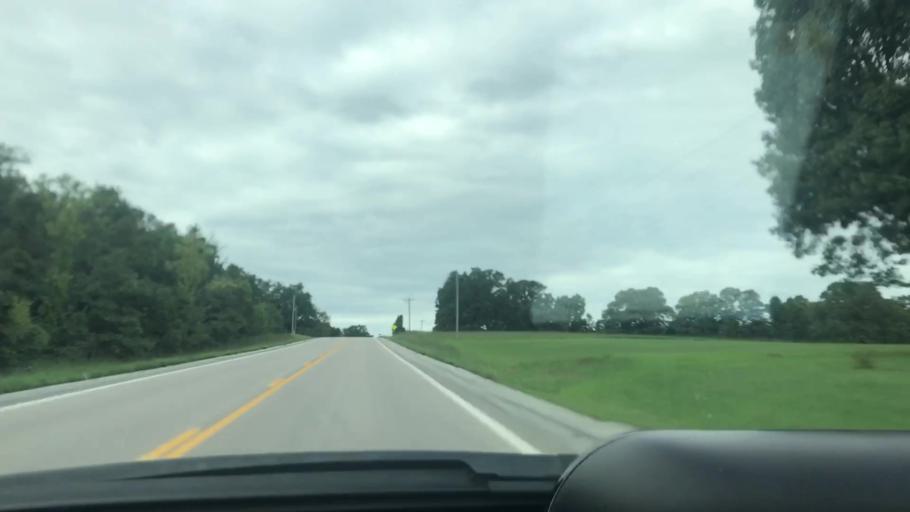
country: US
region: Missouri
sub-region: Benton County
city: Warsaw
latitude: 38.1518
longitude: -93.2947
